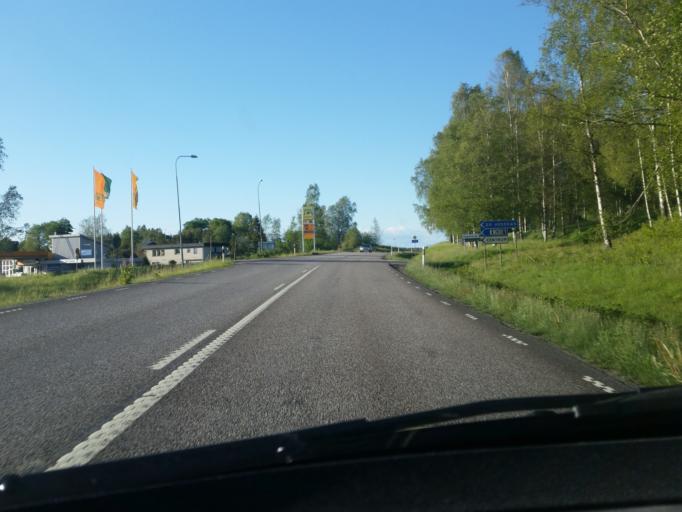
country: SE
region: Vaestra Goetaland
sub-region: Fargelanda Kommun
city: Faergelanda
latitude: 58.5611
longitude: 11.9964
